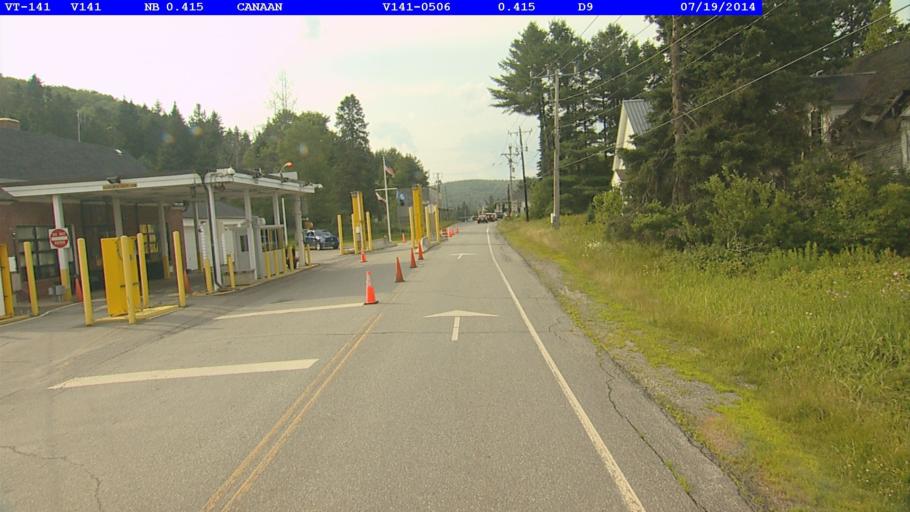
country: US
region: New Hampshire
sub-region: Coos County
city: Colebrook
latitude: 45.0118
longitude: -71.5595
